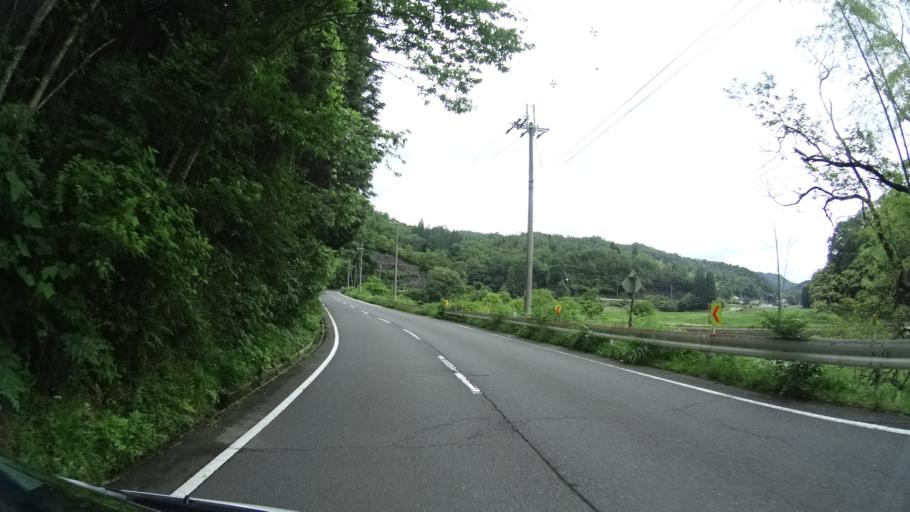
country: JP
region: Kyoto
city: Kameoka
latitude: 35.0798
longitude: 135.4116
